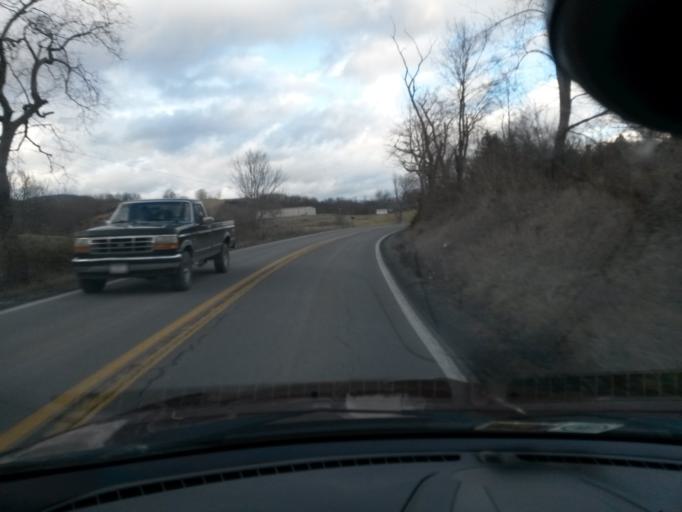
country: US
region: West Virginia
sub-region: Monroe County
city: Union
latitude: 37.5842
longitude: -80.5503
